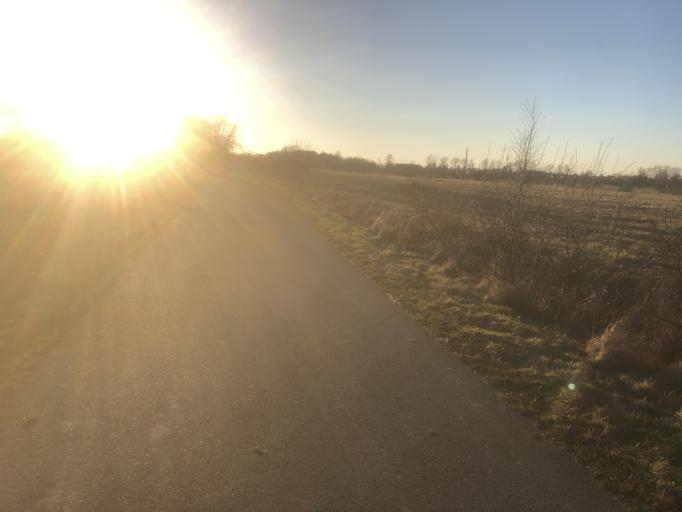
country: DK
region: South Denmark
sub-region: Fredericia Kommune
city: Fredericia
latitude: 55.5876
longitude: 9.7826
